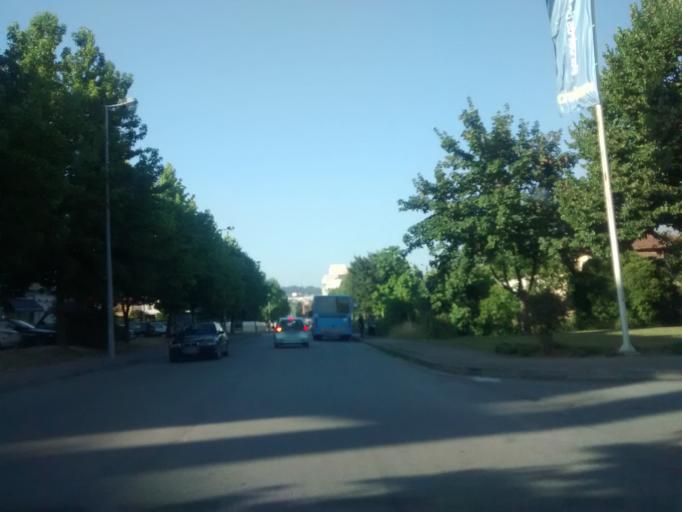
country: PT
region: Braga
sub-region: Braga
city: Braga
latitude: 41.5494
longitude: -8.4026
